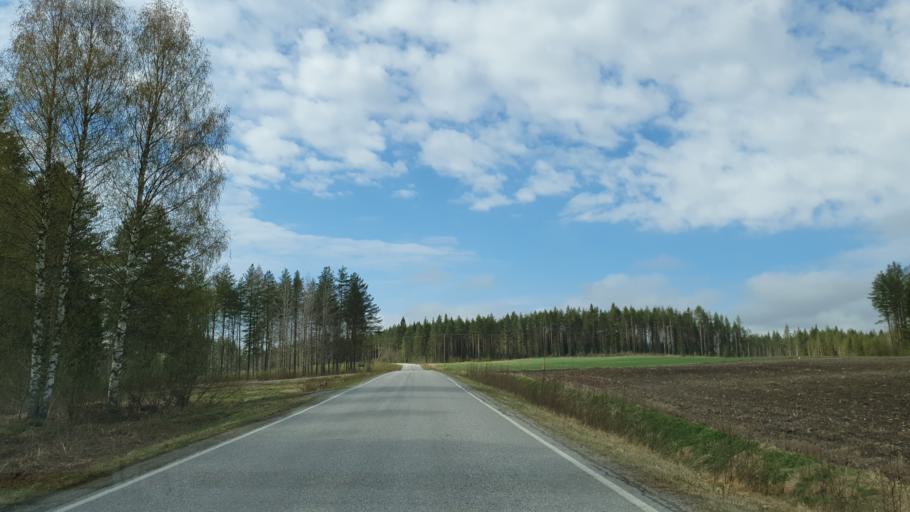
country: FI
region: Kainuu
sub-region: Kehys-Kainuu
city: Kuhmo
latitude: 64.1198
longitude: 29.6918
